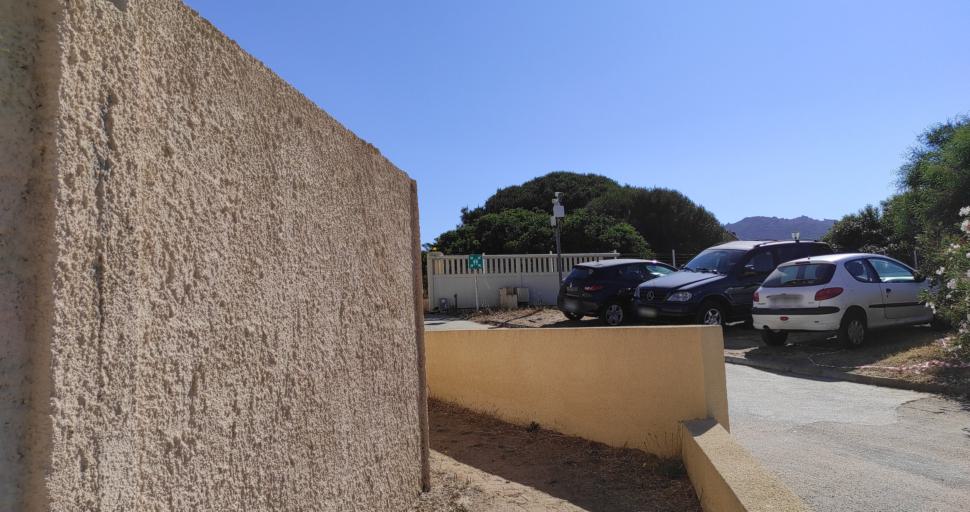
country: FR
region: Corsica
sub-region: Departement de la Corse-du-Sud
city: Alata
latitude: 41.9921
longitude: 8.6701
